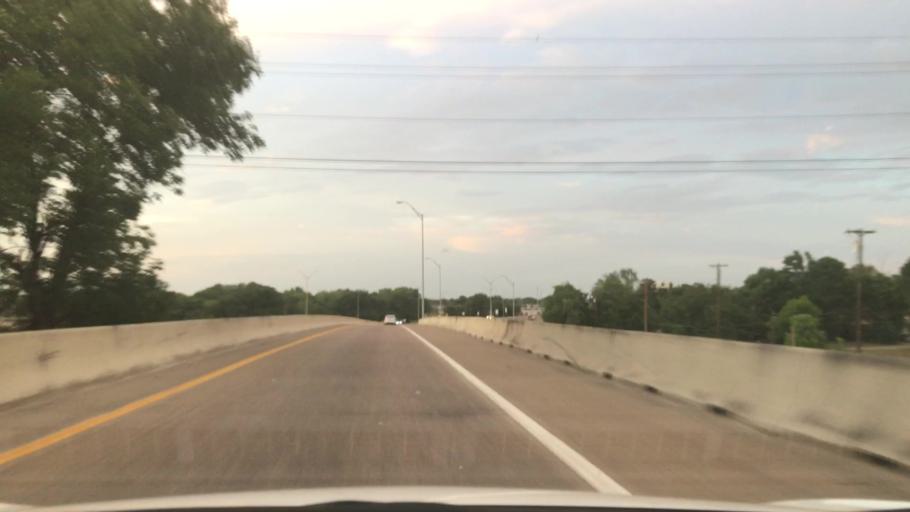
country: US
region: Texas
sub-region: Dallas County
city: Balch Springs
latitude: 32.7044
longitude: -96.6231
